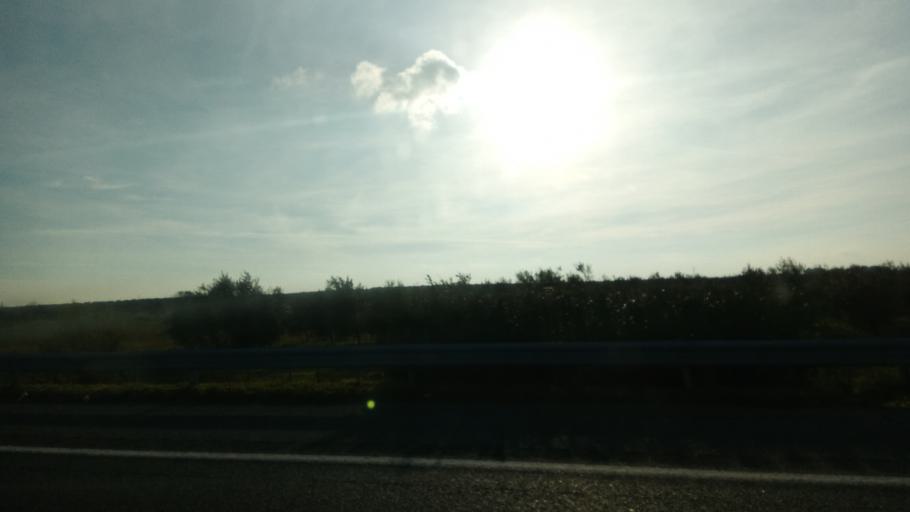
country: IT
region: Apulia
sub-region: Provincia di Foggia
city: San Severo
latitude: 41.6502
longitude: 15.4414
